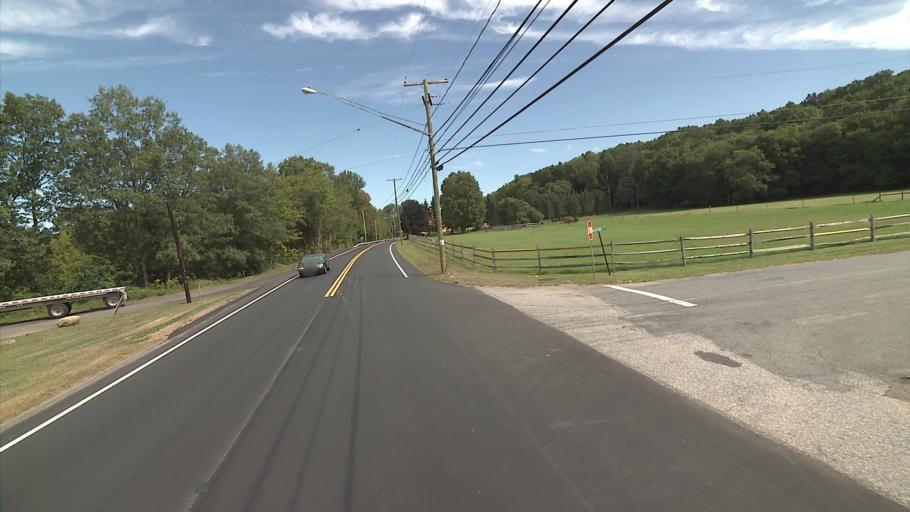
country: US
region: Connecticut
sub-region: Tolland County
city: Storrs
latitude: 41.8415
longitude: -72.3074
